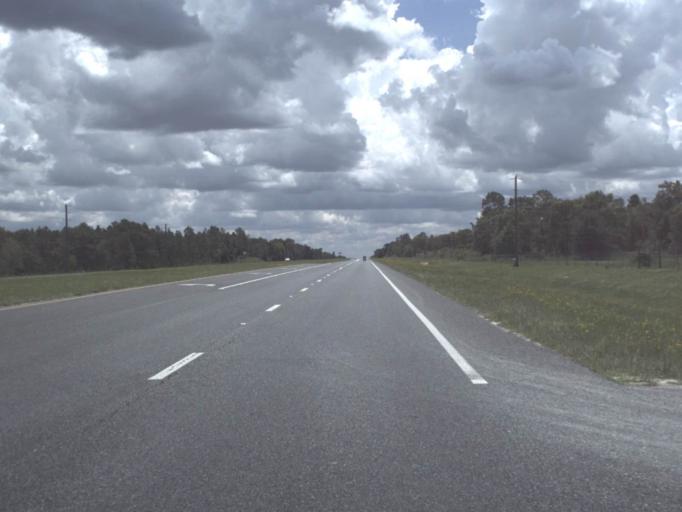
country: US
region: Florida
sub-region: Levy County
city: East Bronson
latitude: 29.4138
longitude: -82.5506
